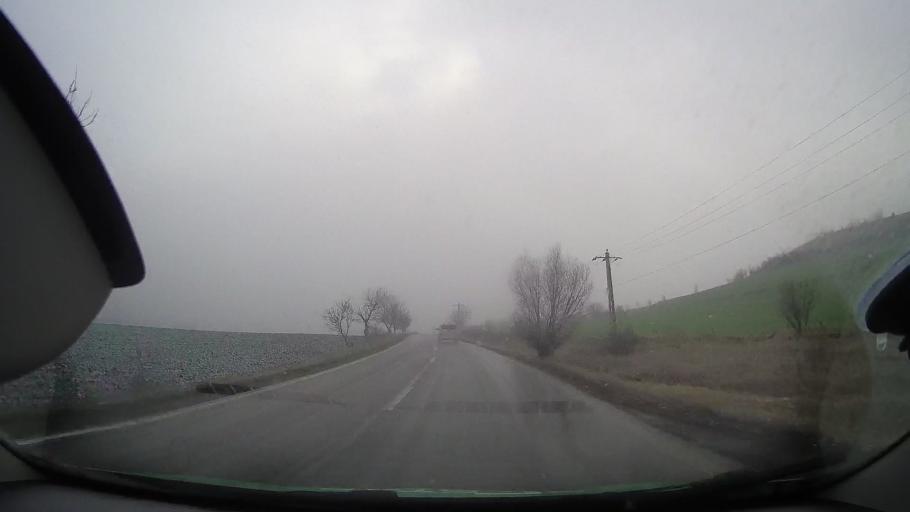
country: RO
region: Mures
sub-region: Municipiul Tarnaveni
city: Tarnaveni
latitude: 46.2921
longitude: 24.3014
